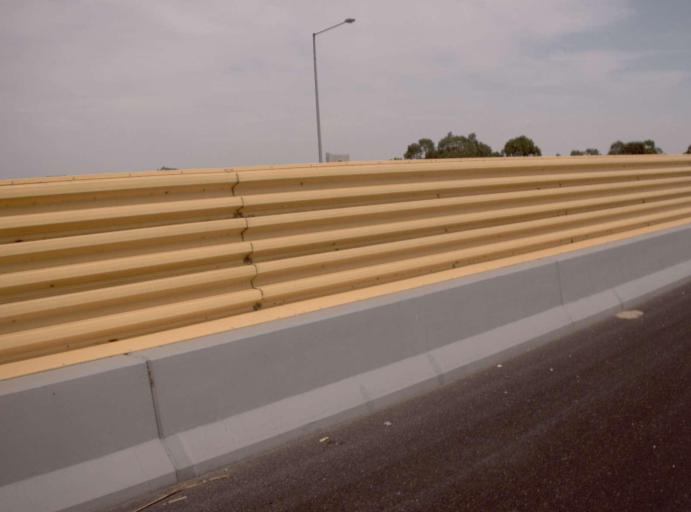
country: AU
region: Victoria
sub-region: Brimbank
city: Sunshine North
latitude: -37.7626
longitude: 144.8202
